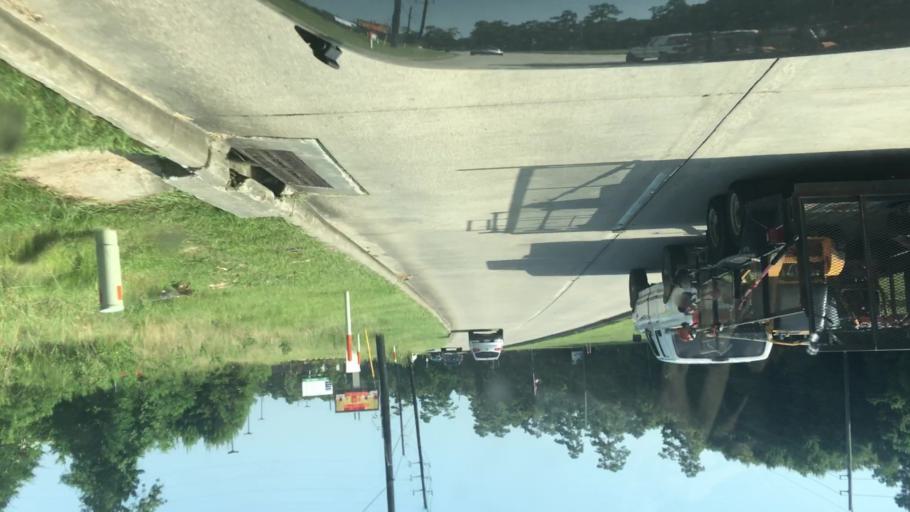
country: US
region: Texas
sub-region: Harris County
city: Atascocita
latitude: 29.9741
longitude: -95.1715
